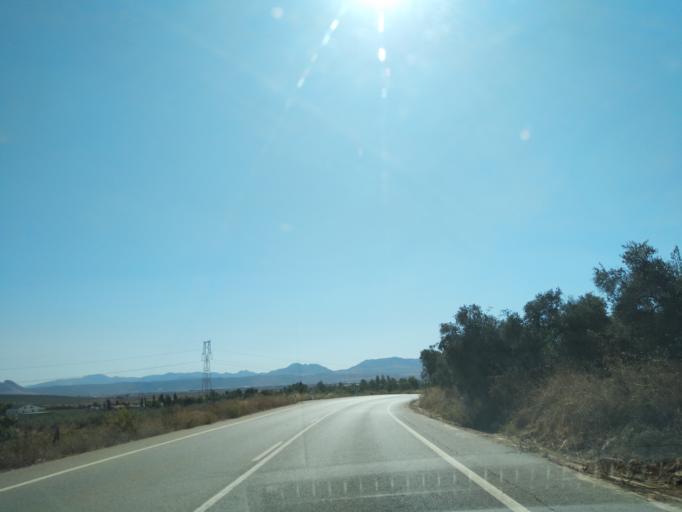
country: ES
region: Andalusia
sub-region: Provincia de Malaga
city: Mollina
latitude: 37.1049
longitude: -4.6372
